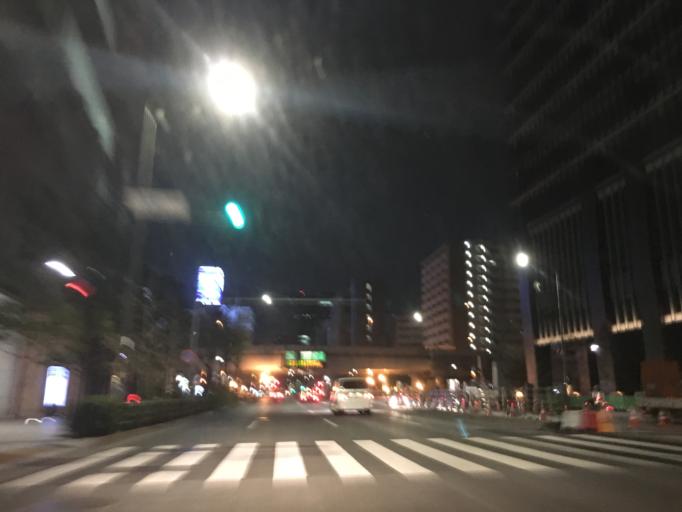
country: JP
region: Tokyo
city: Tokyo
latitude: 35.6883
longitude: 139.7638
